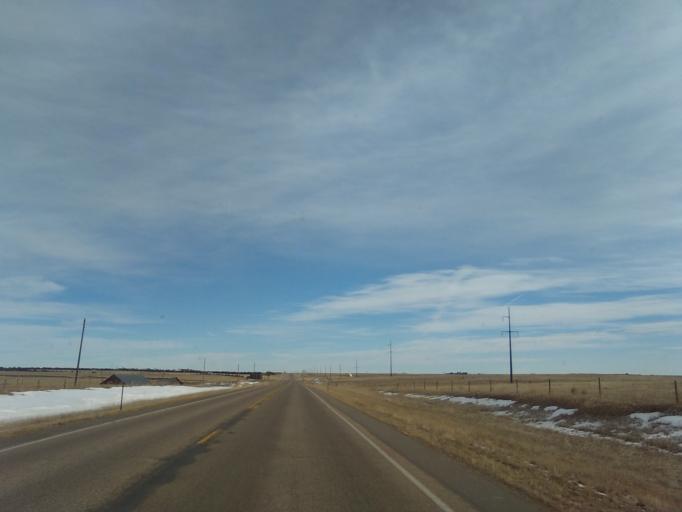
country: US
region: Wyoming
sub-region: Laramie County
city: Ranchettes
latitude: 41.4140
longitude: -104.4254
